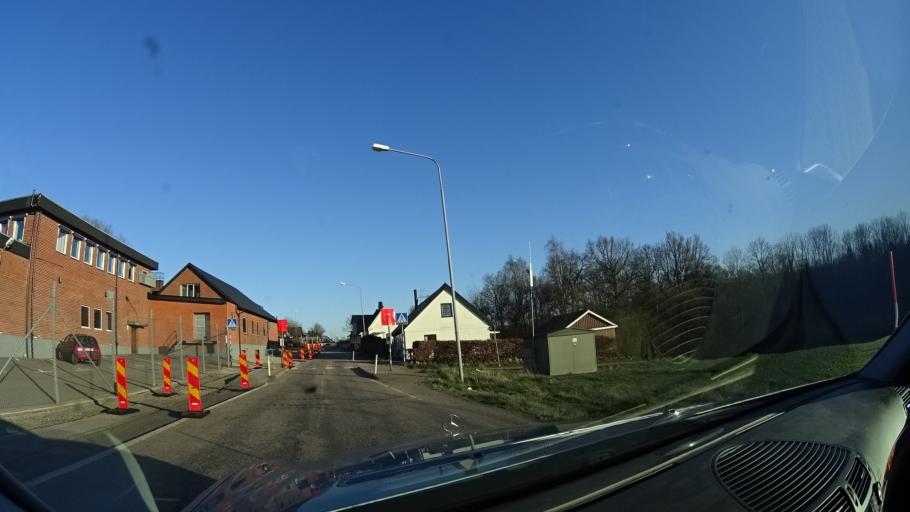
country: SE
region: Skane
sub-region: Bjuvs Kommun
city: Billesholm
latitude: 56.0569
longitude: 12.9938
